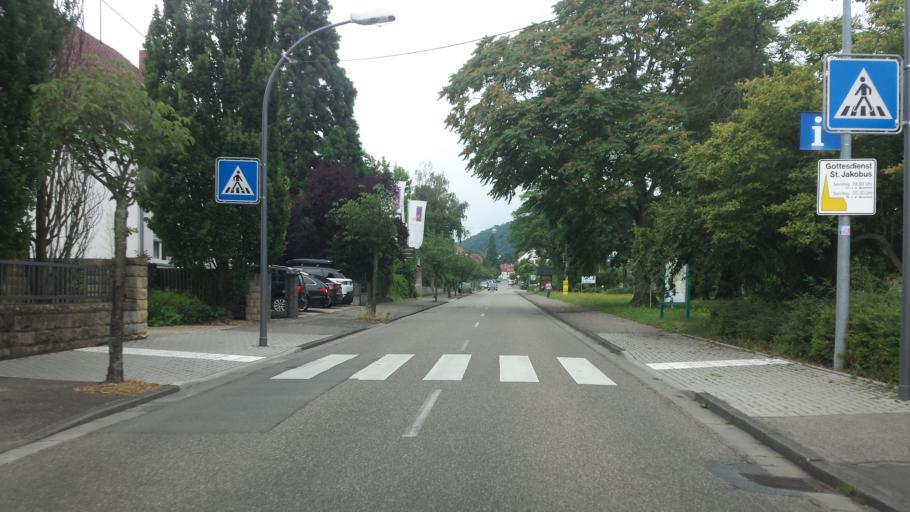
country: DE
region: Rheinland-Pfalz
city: Neustadt
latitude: 49.3418
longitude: 8.1350
